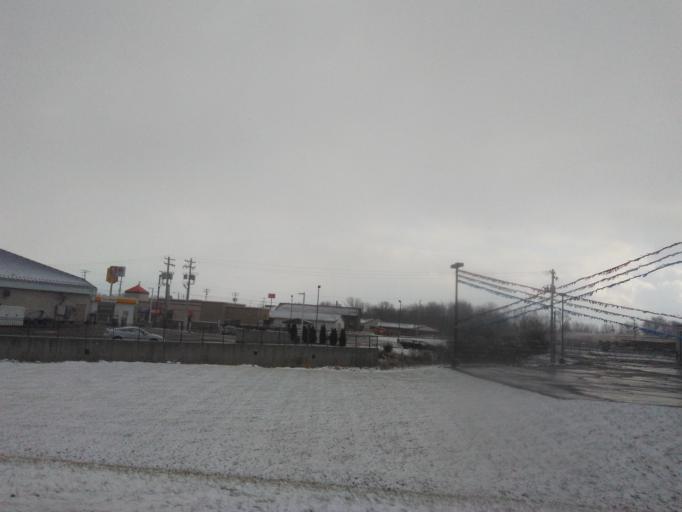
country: US
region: Illinois
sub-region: Bond County
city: Greenville
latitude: 38.8782
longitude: -89.3919
